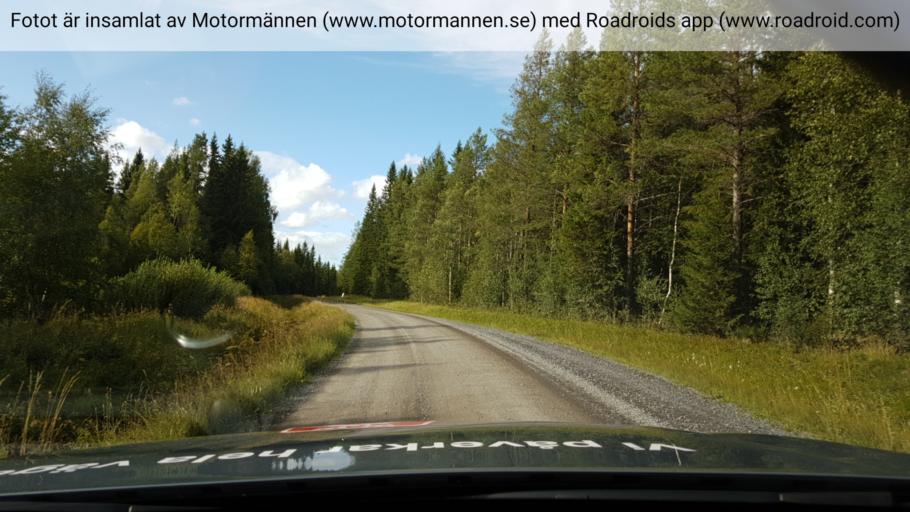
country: SE
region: Jaemtland
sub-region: OEstersunds Kommun
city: Lit
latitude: 63.3151
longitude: 15.2366
